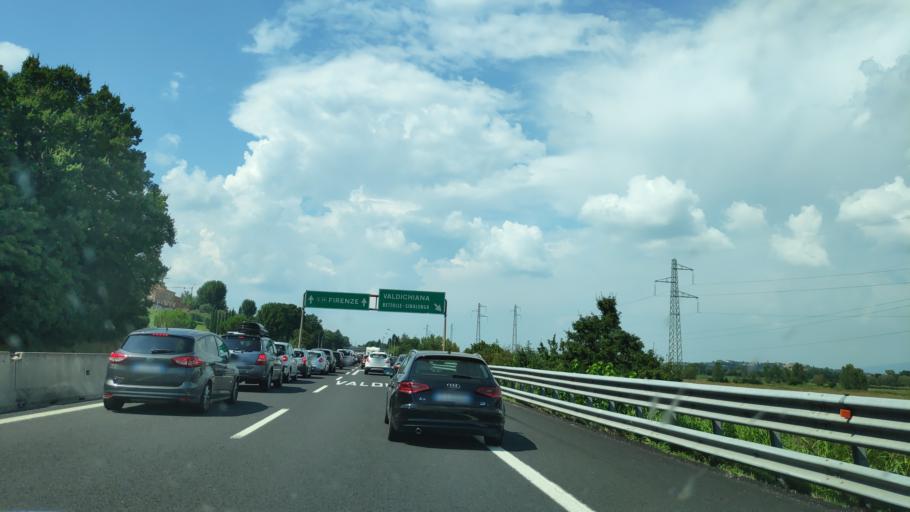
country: IT
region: Tuscany
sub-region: Provincia di Siena
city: Bettolle
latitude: 43.2079
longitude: 11.8119
